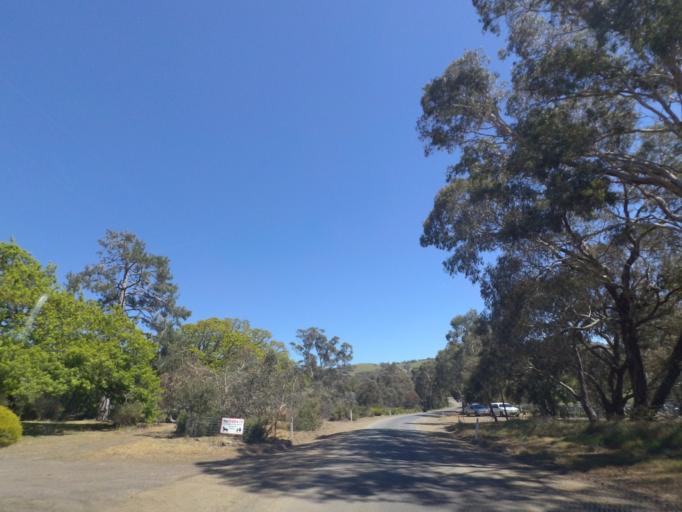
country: AU
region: Victoria
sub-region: Whittlesea
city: Whittlesea
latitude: -37.2901
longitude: 144.9861
